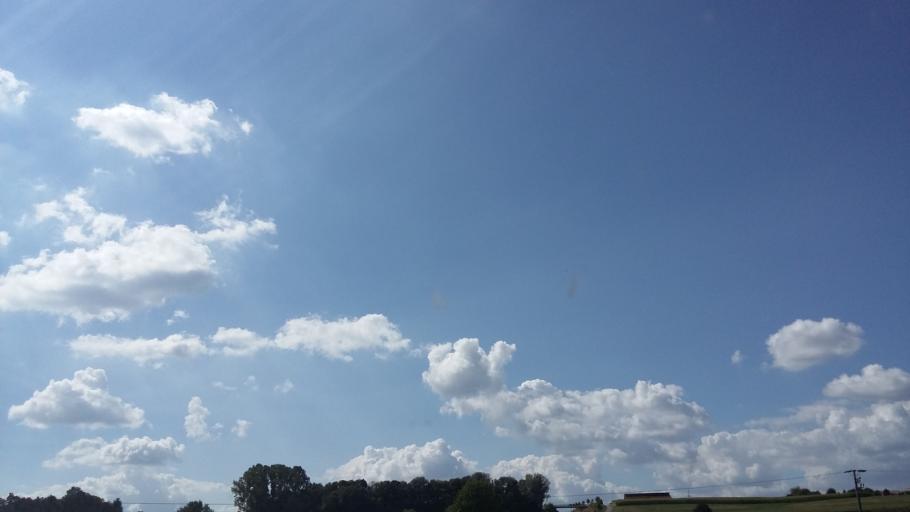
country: DE
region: Bavaria
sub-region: Swabia
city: Holzheim
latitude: 48.3529
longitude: 10.1027
